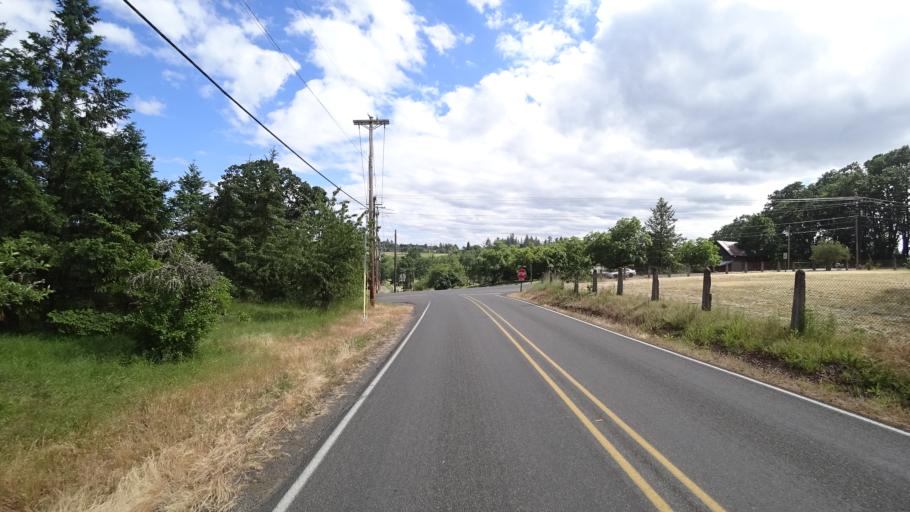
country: US
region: Oregon
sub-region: Washington County
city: Bethany
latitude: 45.5815
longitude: -122.8406
